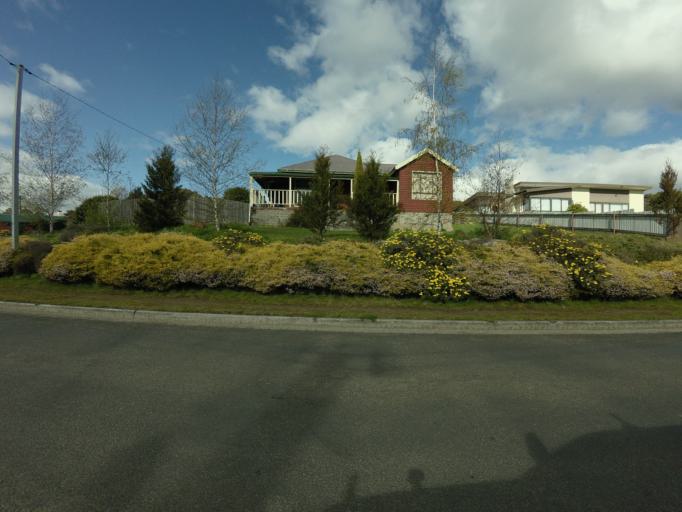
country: AU
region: Tasmania
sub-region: Huon Valley
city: Geeveston
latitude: -43.1650
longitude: 146.9265
